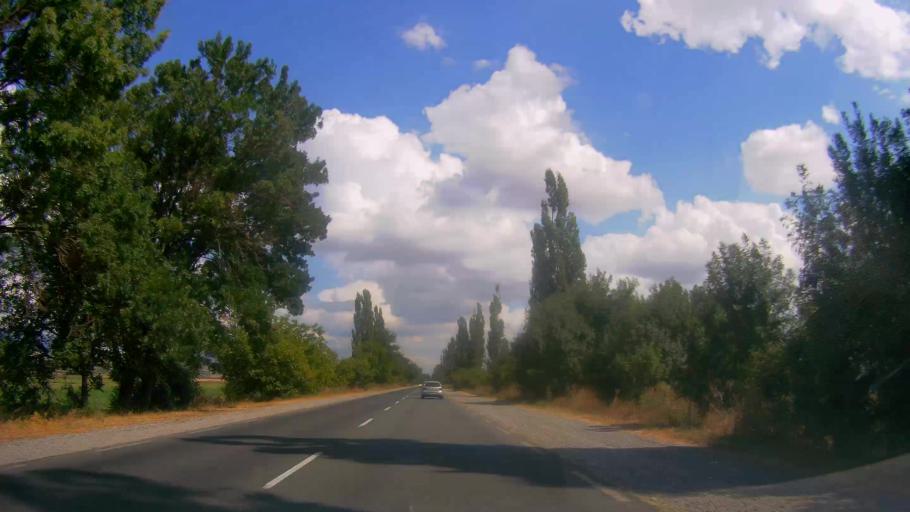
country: BG
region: Sliven
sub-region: Obshtina Sliven
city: Sliven
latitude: 42.6375
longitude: 26.2582
